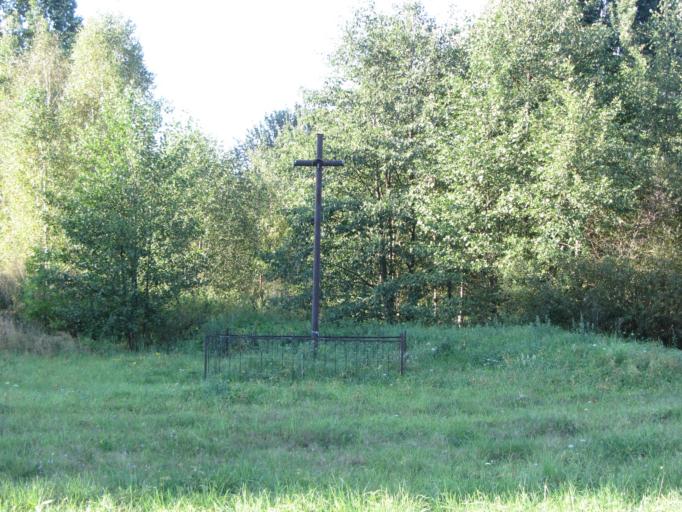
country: BY
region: Grodnenskaya
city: Iwye
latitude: 54.1999
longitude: 25.6929
